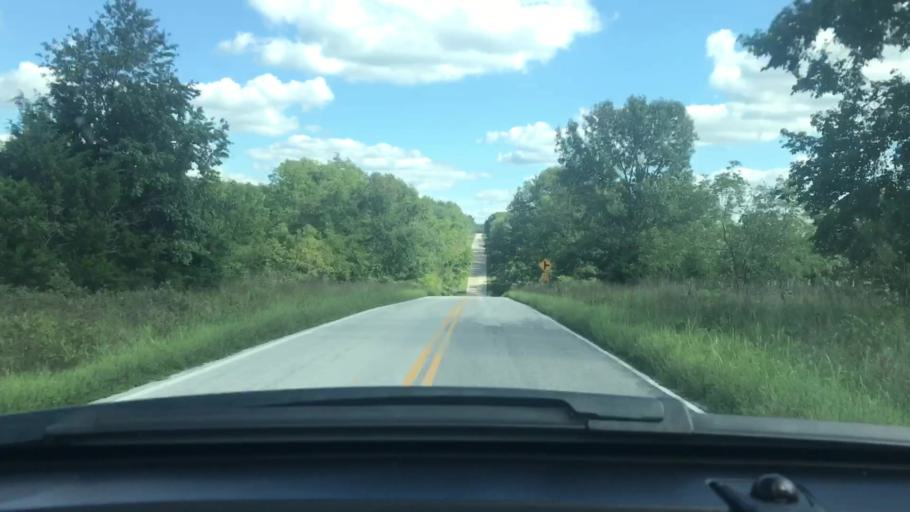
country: US
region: Missouri
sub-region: Wright County
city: Hartville
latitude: 37.3861
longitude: -92.4433
